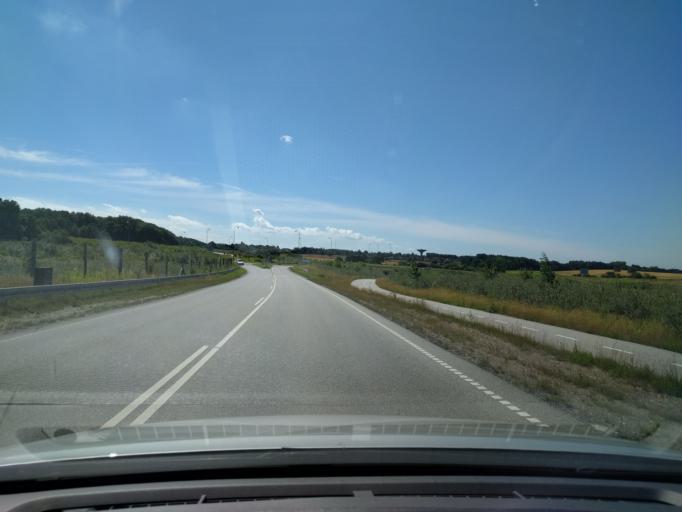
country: DK
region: Zealand
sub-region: Naestved Kommune
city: Fensmark
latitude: 55.2466
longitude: 11.7989
